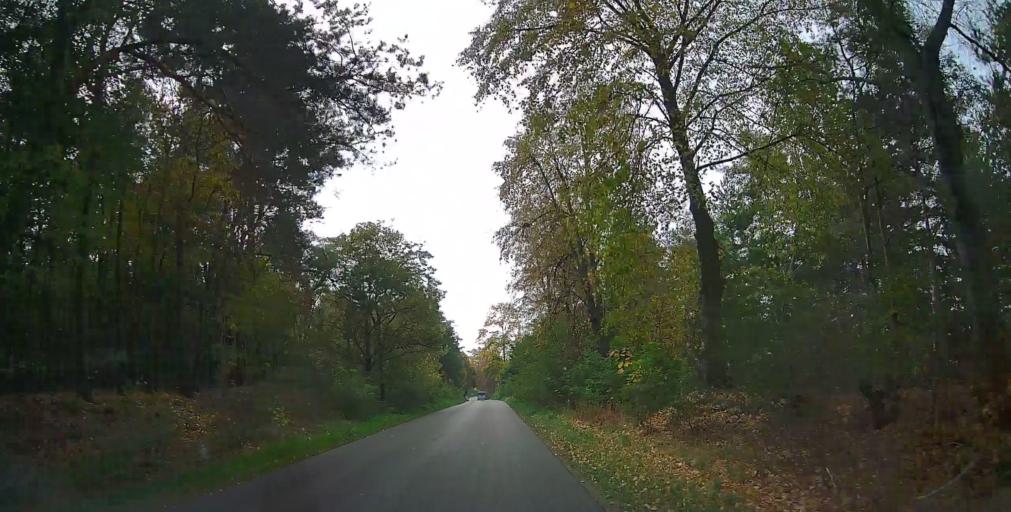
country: PL
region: Masovian Voivodeship
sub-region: Powiat grojecki
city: Mogielnica
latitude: 51.6716
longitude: 20.7119
